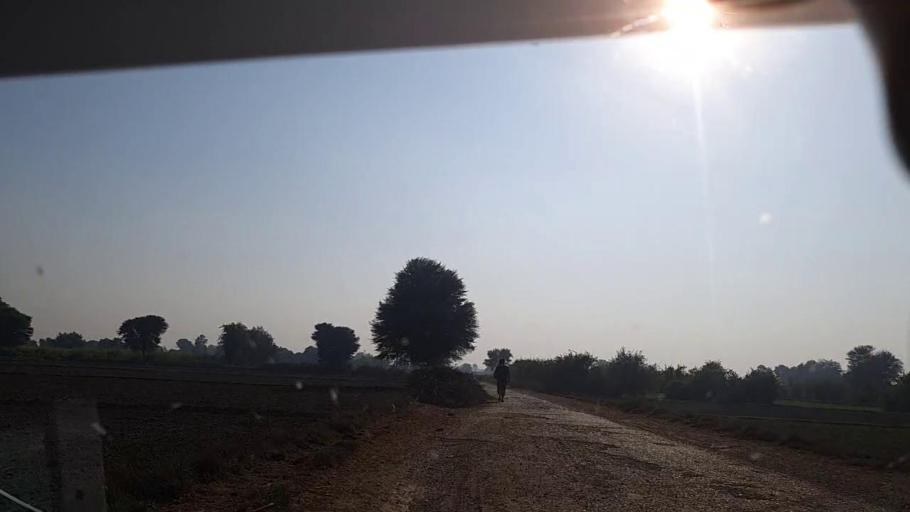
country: PK
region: Sindh
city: Hingorja
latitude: 27.2171
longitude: 68.2655
